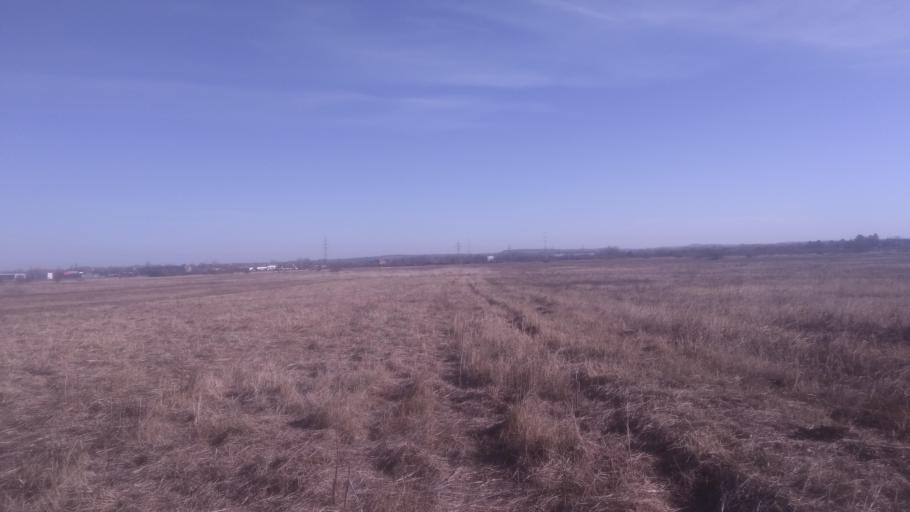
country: HU
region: Pest
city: Budakalasz
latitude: 47.6373
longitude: 19.0488
